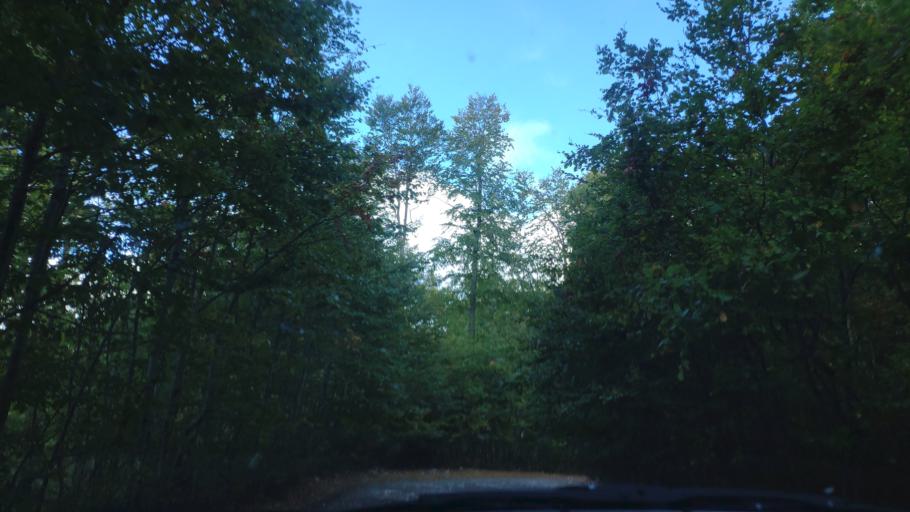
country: GR
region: West Macedonia
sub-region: Nomos Kastorias
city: Nestorio
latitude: 40.3120
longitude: 20.9148
